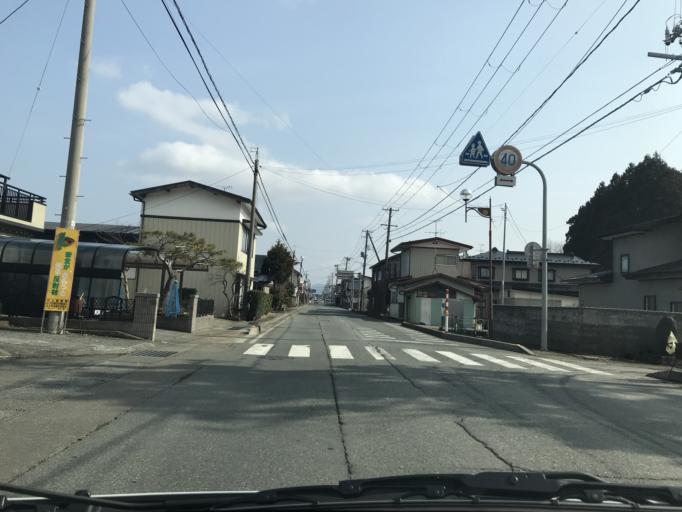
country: JP
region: Iwate
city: Kitakami
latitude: 39.2963
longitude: 141.0715
